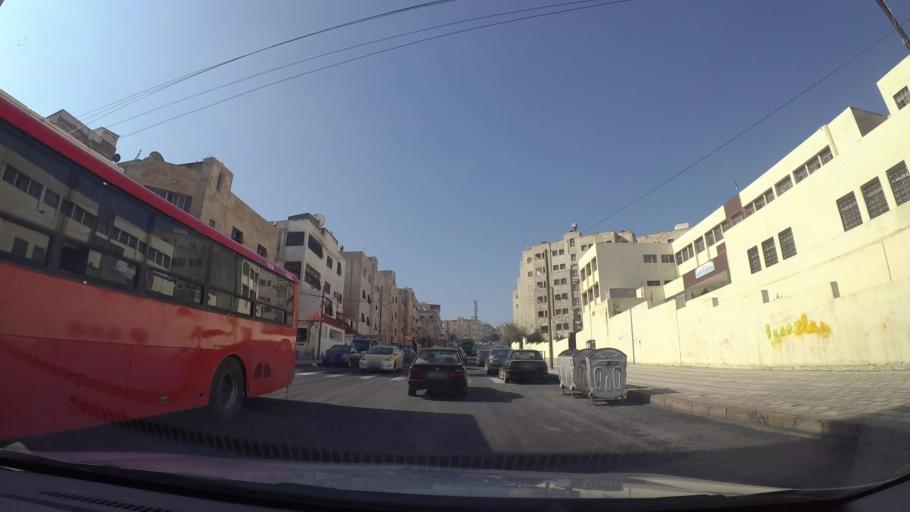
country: JO
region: Amman
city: Amman
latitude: 31.9336
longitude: 35.9086
